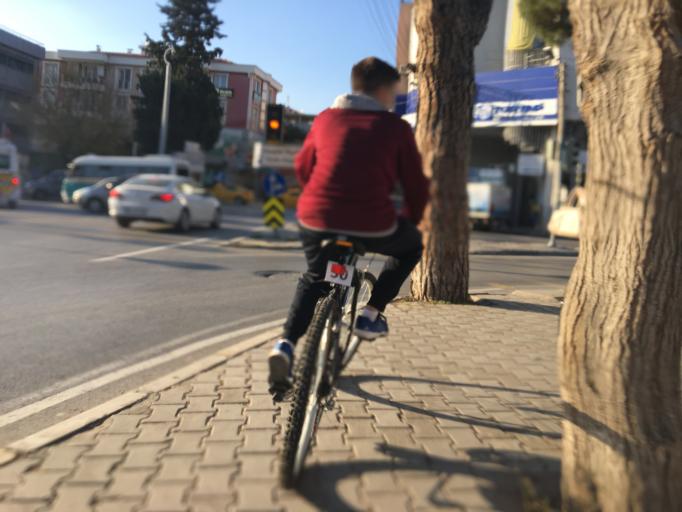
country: TR
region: Izmir
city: Buca
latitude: 38.3837
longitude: 27.1689
